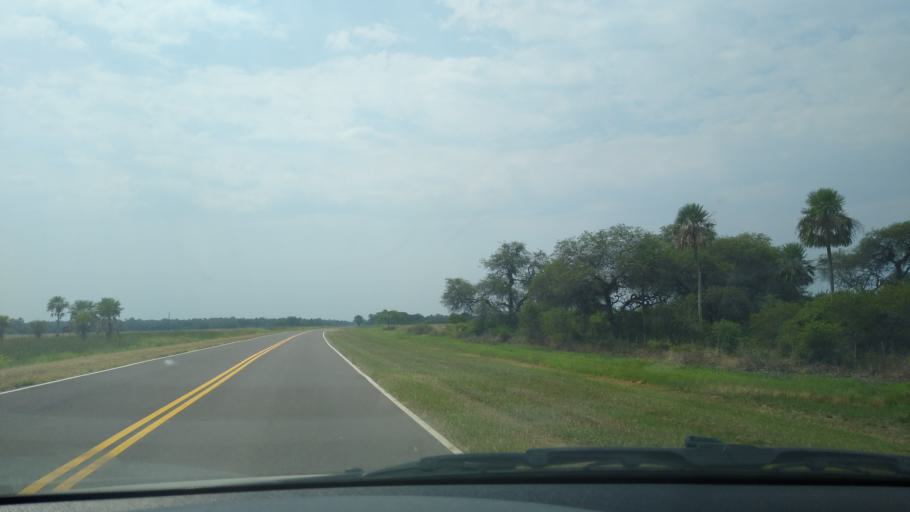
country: AR
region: Chaco
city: Margarita Belen
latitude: -27.0690
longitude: -58.9629
